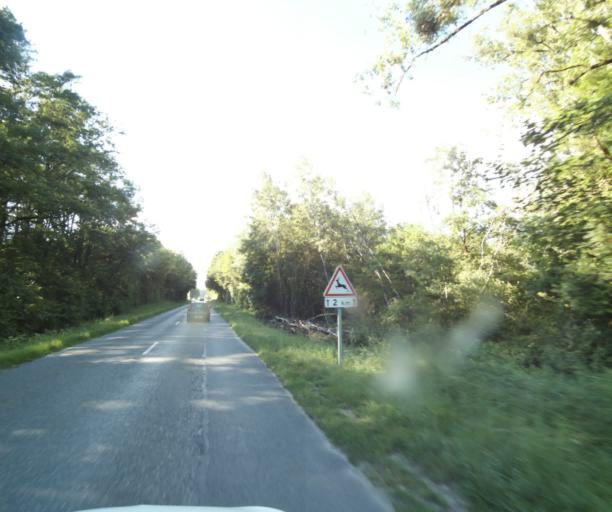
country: FR
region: Rhone-Alpes
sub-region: Departement de la Haute-Savoie
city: Douvaine
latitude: 46.3177
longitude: 6.2972
